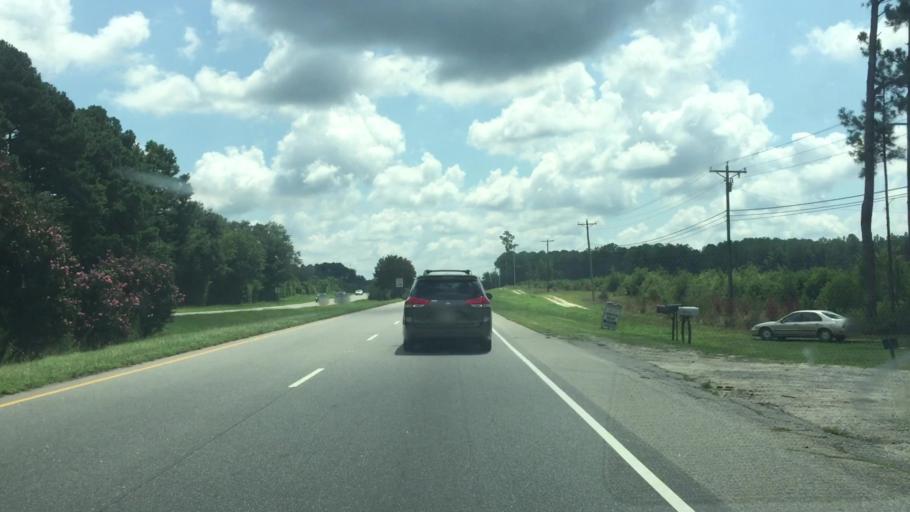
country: US
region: North Carolina
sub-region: Scotland County
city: Laurel Hill
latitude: 34.8122
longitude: -79.5600
